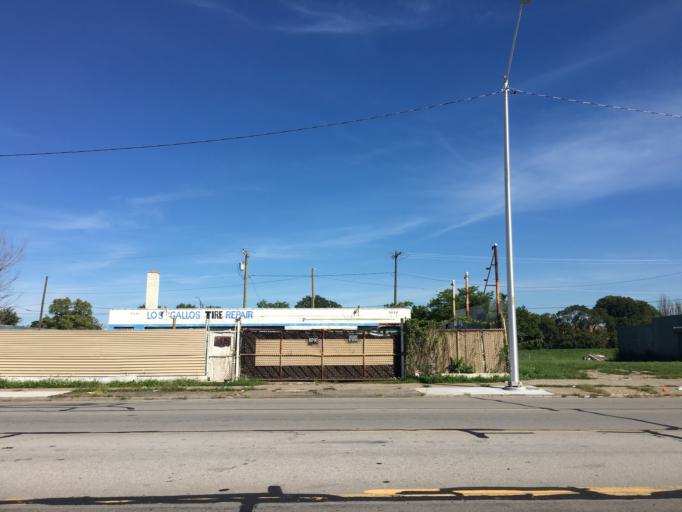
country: US
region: Michigan
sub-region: Wayne County
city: River Rouge
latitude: 42.3060
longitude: -83.1048
